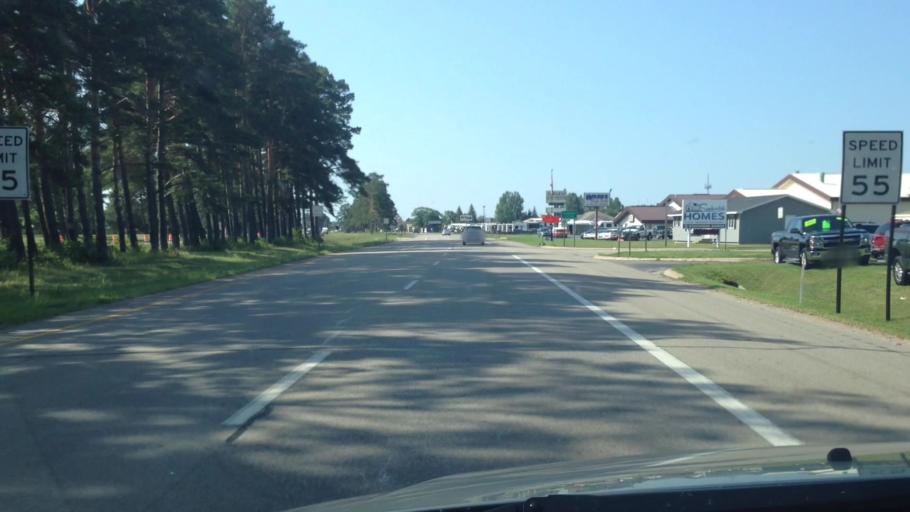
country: US
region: Michigan
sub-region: Delta County
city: Escanaba
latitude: 45.7866
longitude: -87.0825
